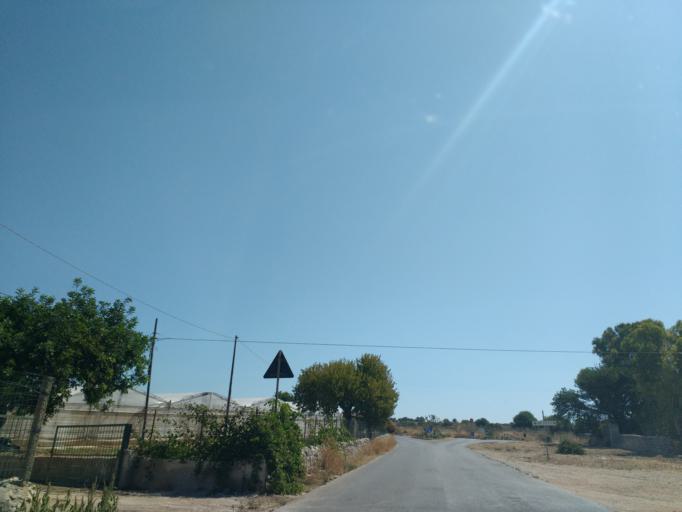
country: IT
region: Sicily
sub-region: Ragusa
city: Cava d'Aliga
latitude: 36.7529
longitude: 14.7021
